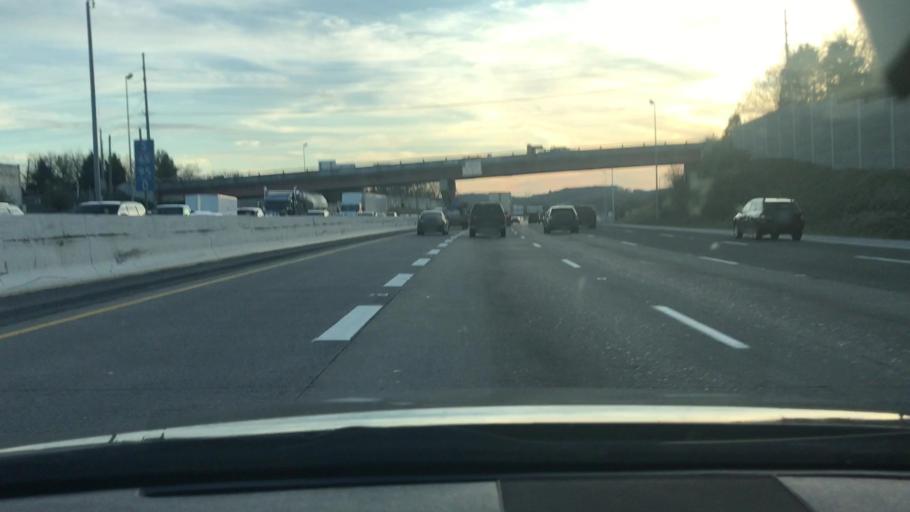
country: US
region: Tennessee
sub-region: Davidson County
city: Goodlettsville
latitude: 36.2987
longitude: -86.7130
